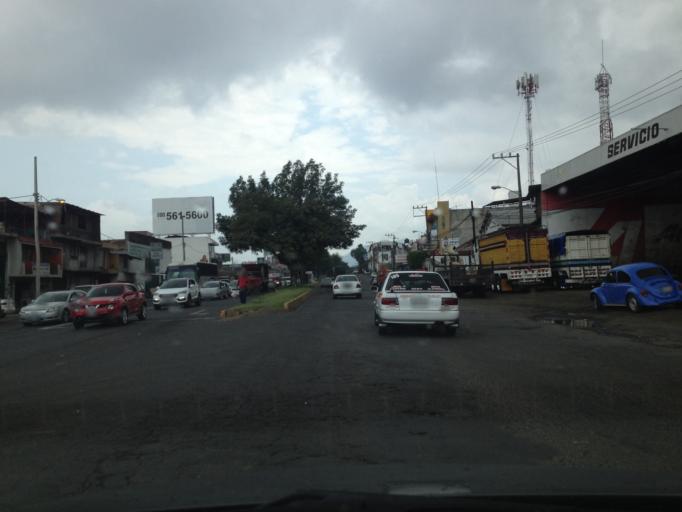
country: MX
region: Michoacan
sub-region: Uruapan
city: Uruapan
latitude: 19.4271
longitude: -102.0389
